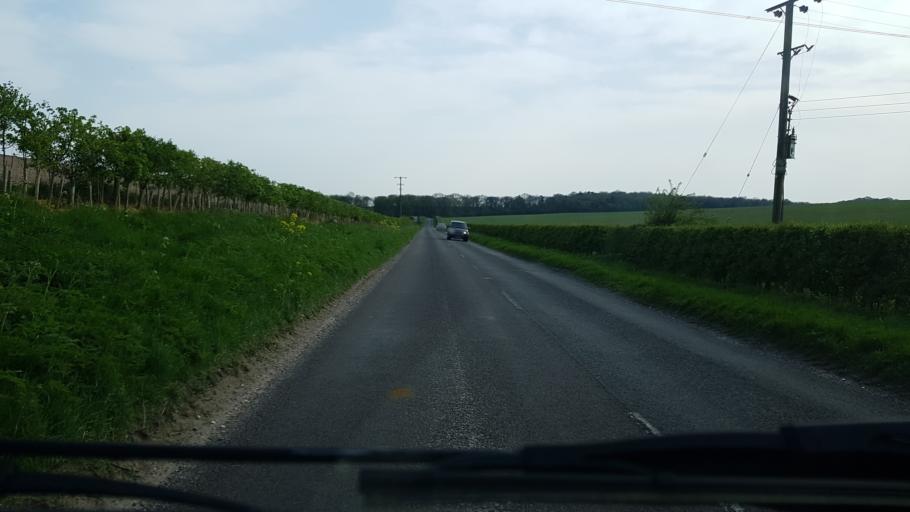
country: GB
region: England
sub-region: Hampshire
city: Kingsclere
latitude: 51.2973
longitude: -1.2662
